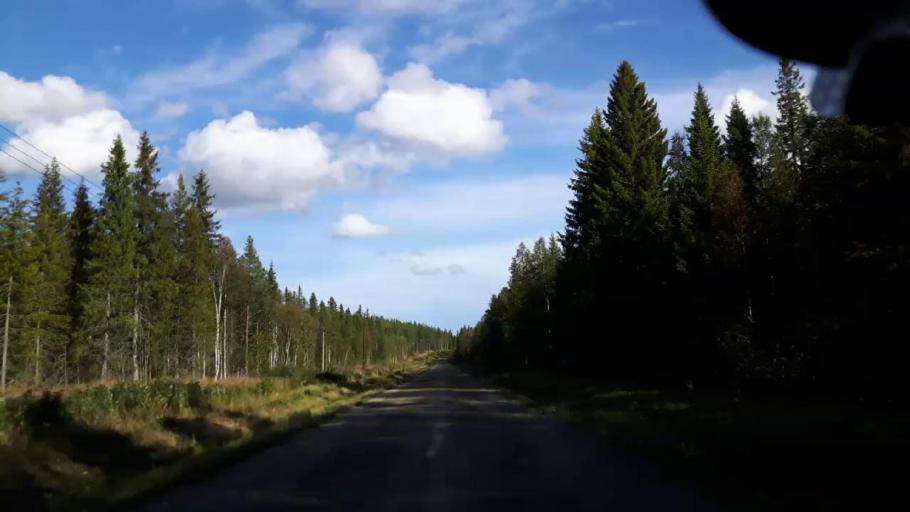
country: SE
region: Jaemtland
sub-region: Ragunda Kommun
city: Hammarstrand
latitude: 63.4355
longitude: 16.0232
